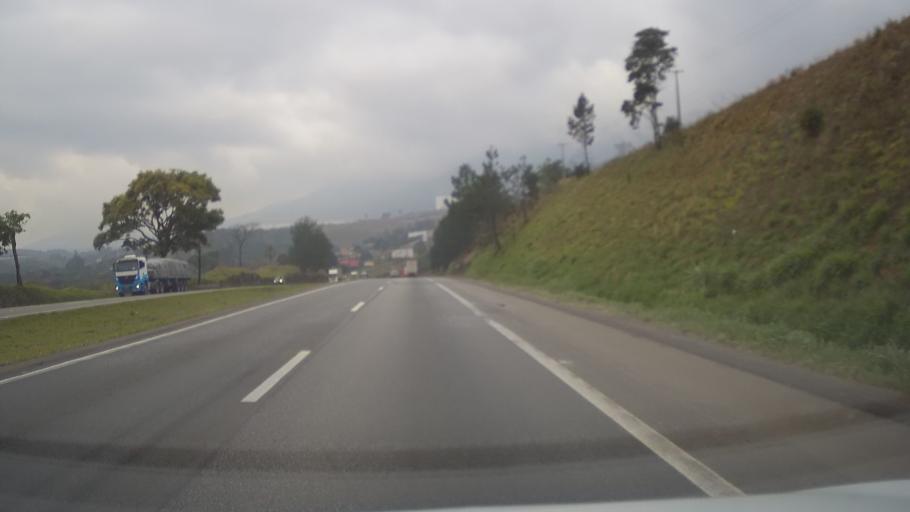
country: BR
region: Minas Gerais
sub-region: Extrema
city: Extrema
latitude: -22.8816
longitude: -46.3803
